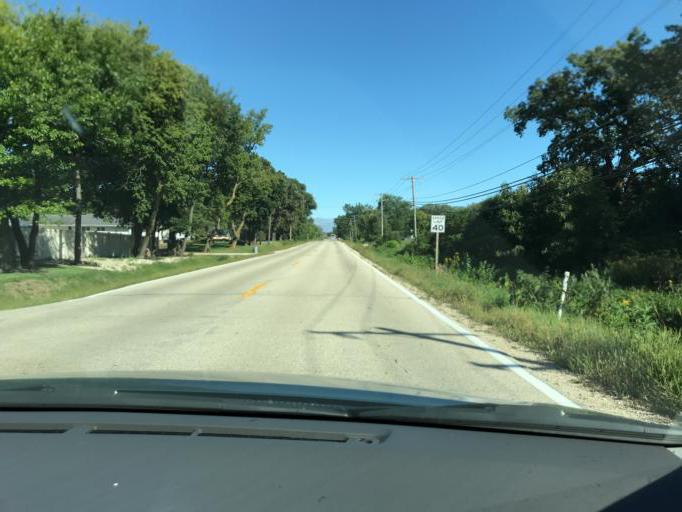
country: US
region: Illinois
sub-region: Lake County
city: Winthrop Harbor
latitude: 42.5223
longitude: -87.8430
